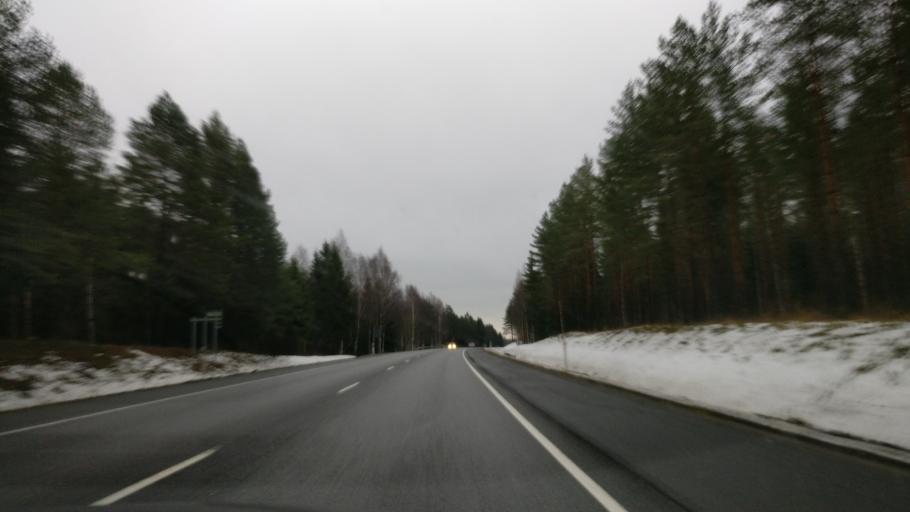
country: FI
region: Uusimaa
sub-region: Raaseporin
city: Karis
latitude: 60.0668
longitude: 23.8173
